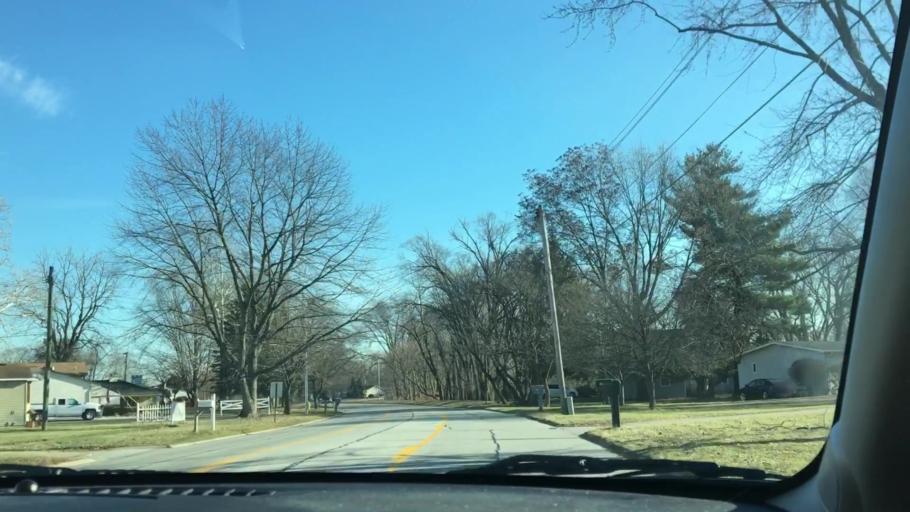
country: US
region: Michigan
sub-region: Wayne County
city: Livonia
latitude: 42.3472
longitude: -83.3652
